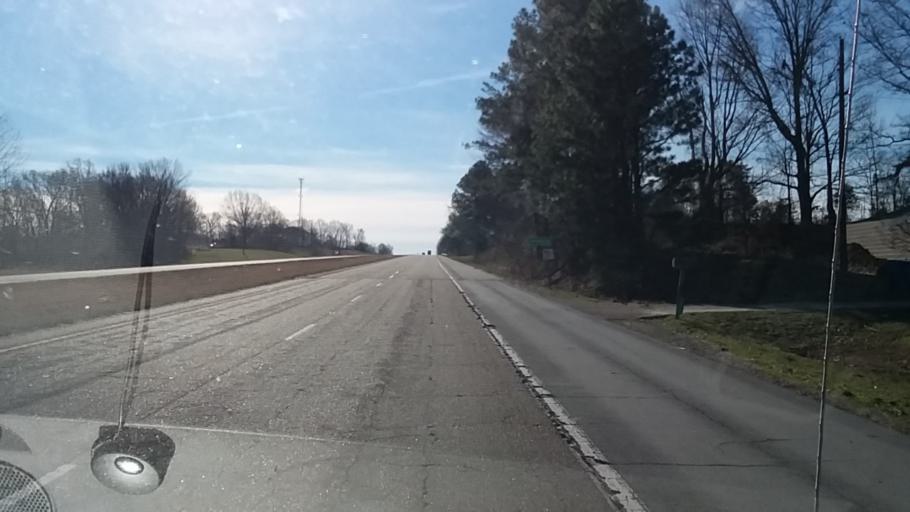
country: US
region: Tennessee
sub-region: Lauderdale County
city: Halls
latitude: 35.9137
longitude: -89.2677
